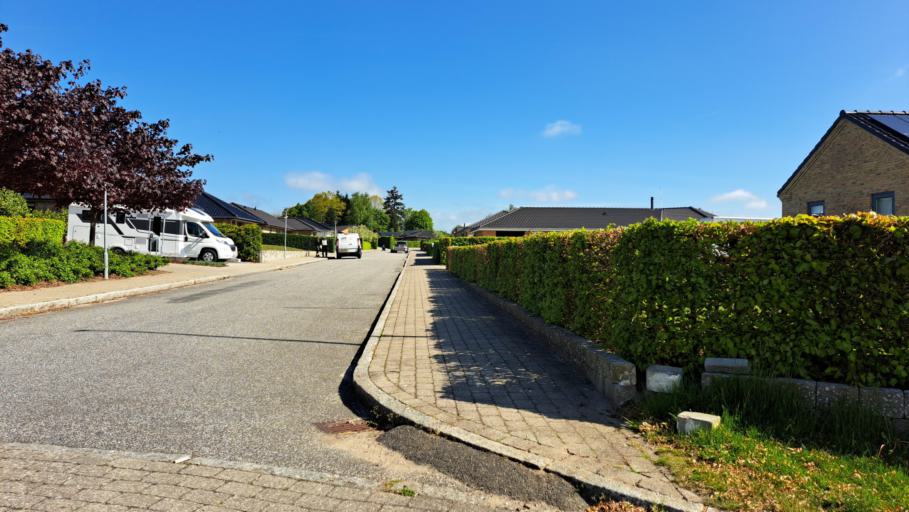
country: DK
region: Central Jutland
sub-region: Hedensted Kommune
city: Hedensted
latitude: 55.7995
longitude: 9.6455
